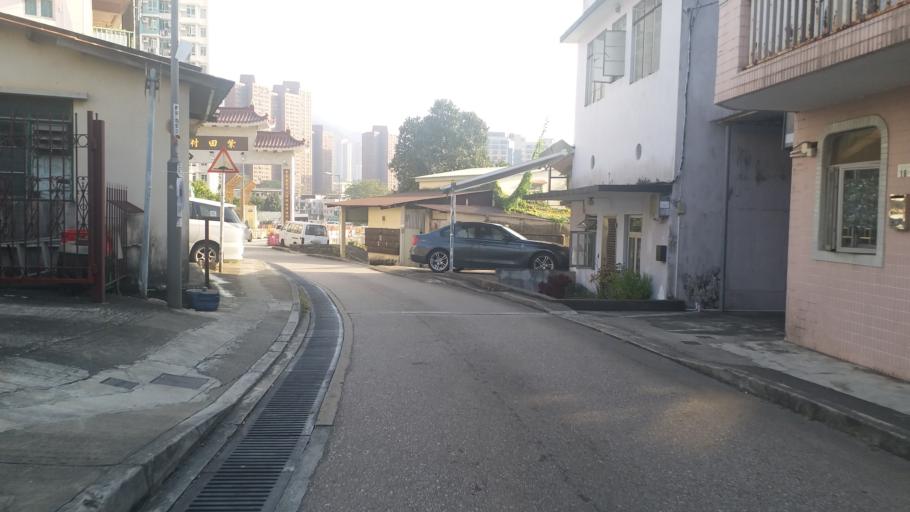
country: HK
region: Tuen Mun
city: Tuen Mun
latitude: 22.4153
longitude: 113.9742
